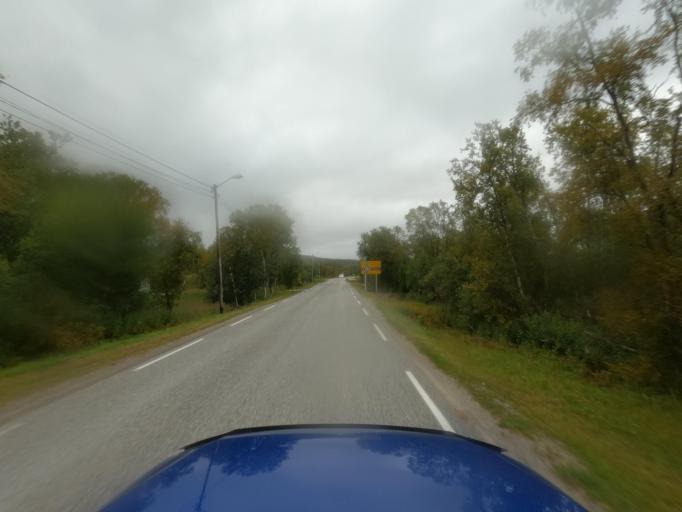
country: NO
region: Finnmark Fylke
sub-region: Porsanger
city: Lakselv
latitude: 70.4719
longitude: 25.0751
